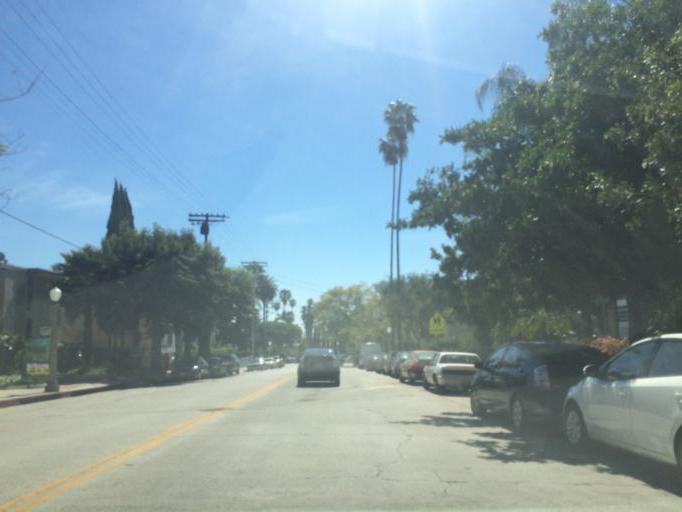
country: US
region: California
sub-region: Los Angeles County
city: Hollywood
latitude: 34.1075
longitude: -118.3217
